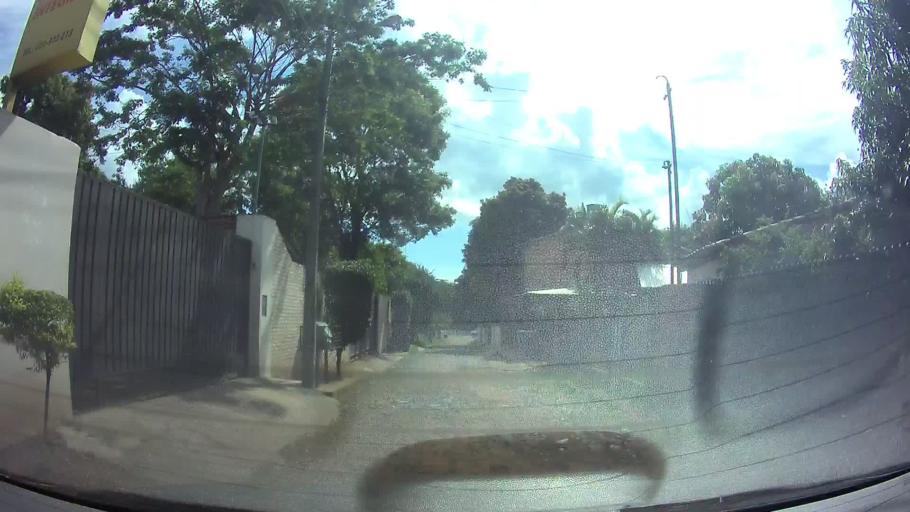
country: PY
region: Central
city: San Antonio
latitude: -25.4266
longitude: -57.5364
